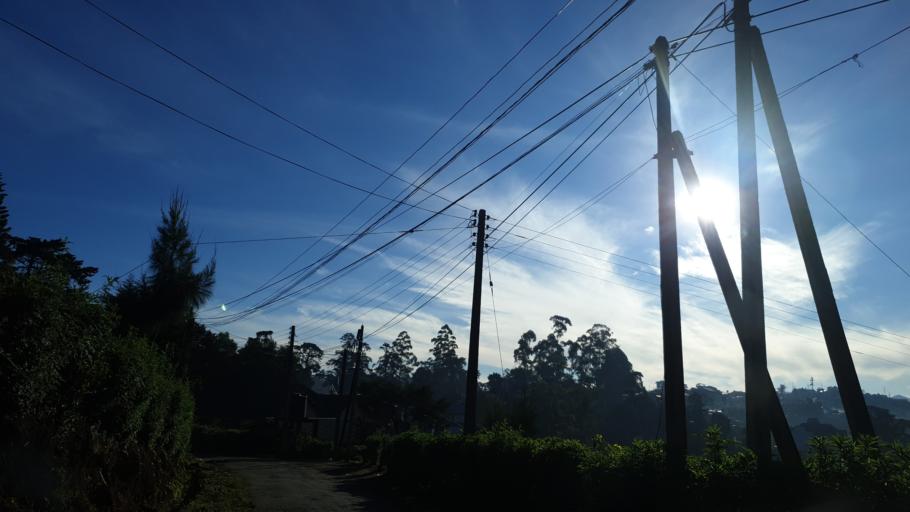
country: LK
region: Central
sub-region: Nuwara Eliya District
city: Nuwara Eliya
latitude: 6.9605
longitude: 80.7668
